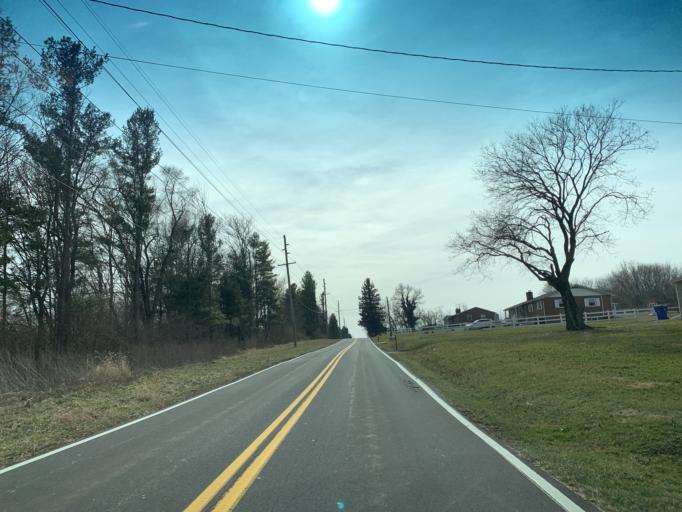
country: US
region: Maryland
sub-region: Frederick County
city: Buckeystown
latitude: 39.3474
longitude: -77.4498
